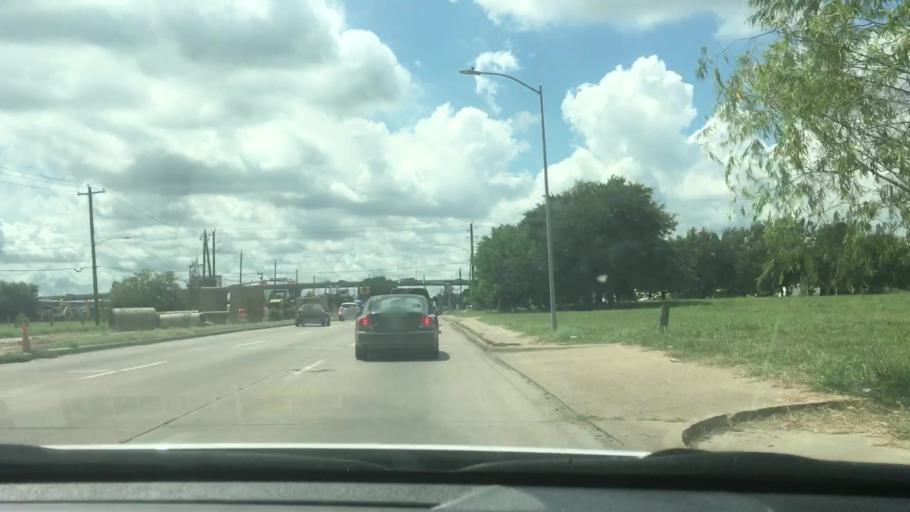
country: US
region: Texas
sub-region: Harris County
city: Bellaire
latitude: 29.6525
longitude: -95.4640
